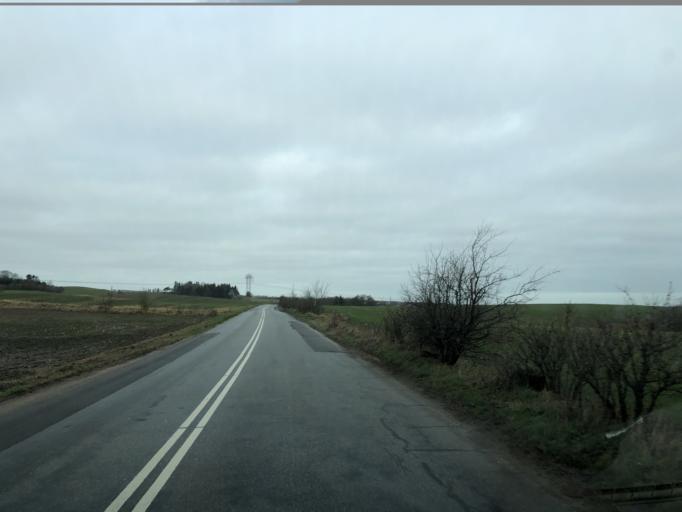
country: DK
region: Central Jutland
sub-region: Viborg Kommune
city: Stoholm
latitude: 56.4656
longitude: 9.1449
